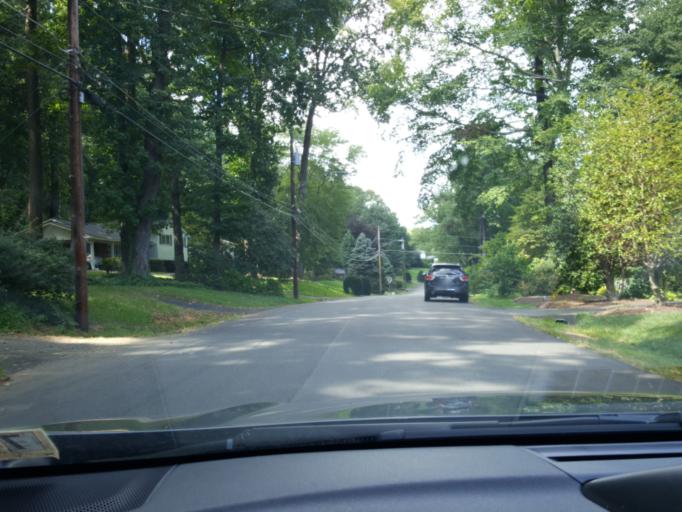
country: US
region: Virginia
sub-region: Fairfax County
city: Annandale
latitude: 38.8168
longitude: -77.1826
